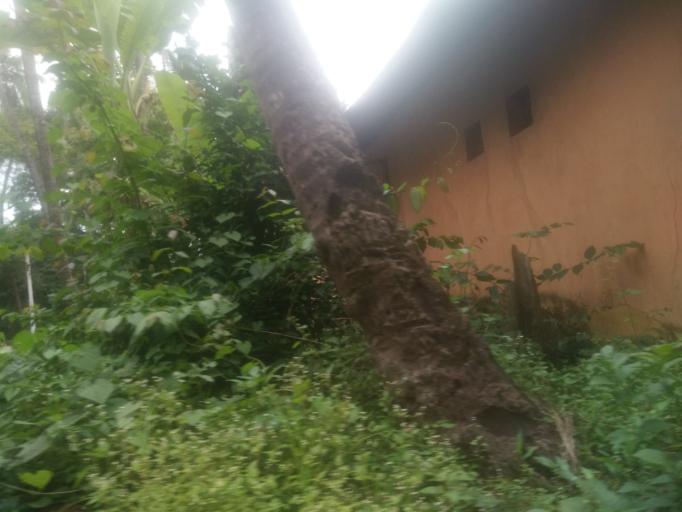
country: IN
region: Goa
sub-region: South Goa
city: Varca
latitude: 15.2123
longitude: 73.9506
